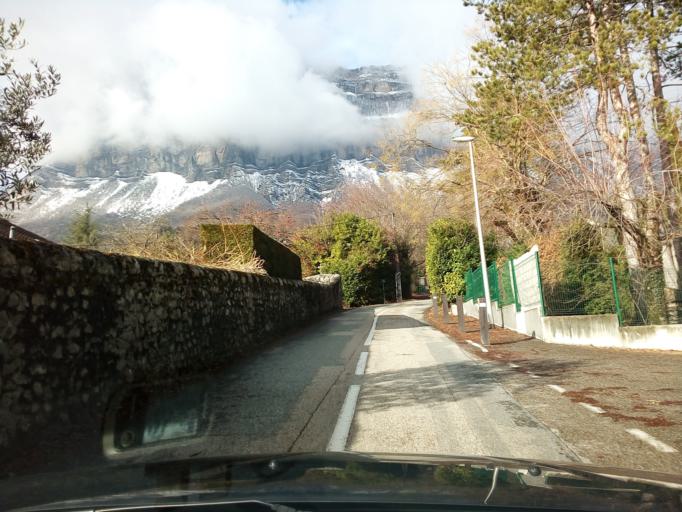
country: FR
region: Rhone-Alpes
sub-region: Departement de l'Isere
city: Meylan
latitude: 45.2240
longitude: 5.7861
